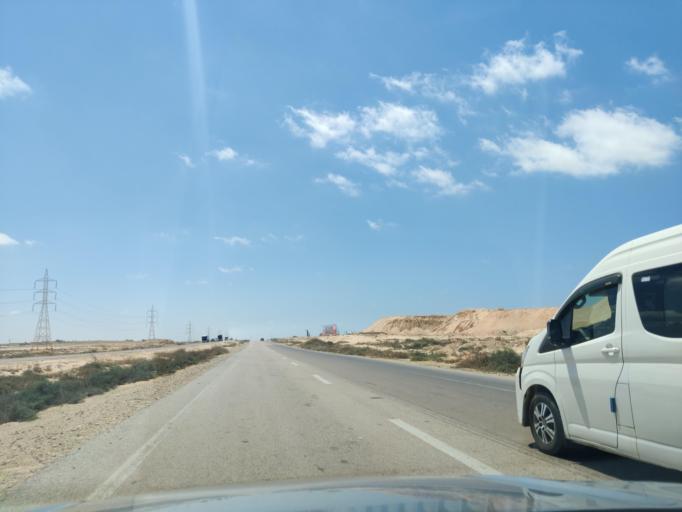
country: EG
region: Muhafazat Matruh
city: Al `Alamayn
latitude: 31.0646
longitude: 28.1913
